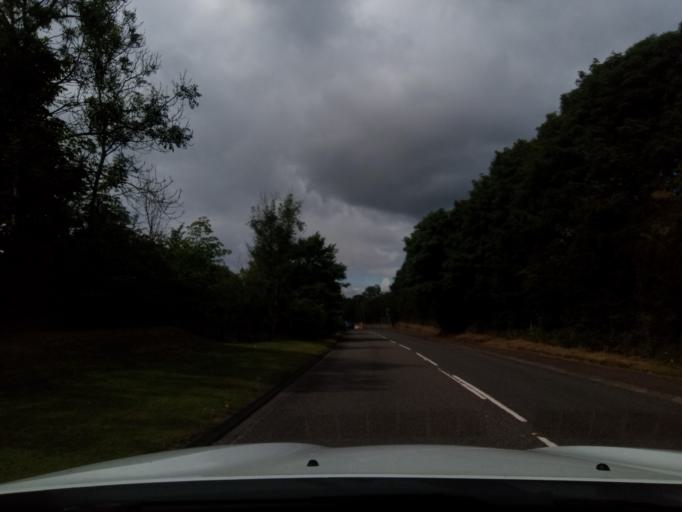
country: GB
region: Scotland
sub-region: Fife
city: Oakley
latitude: 56.0595
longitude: -3.5473
